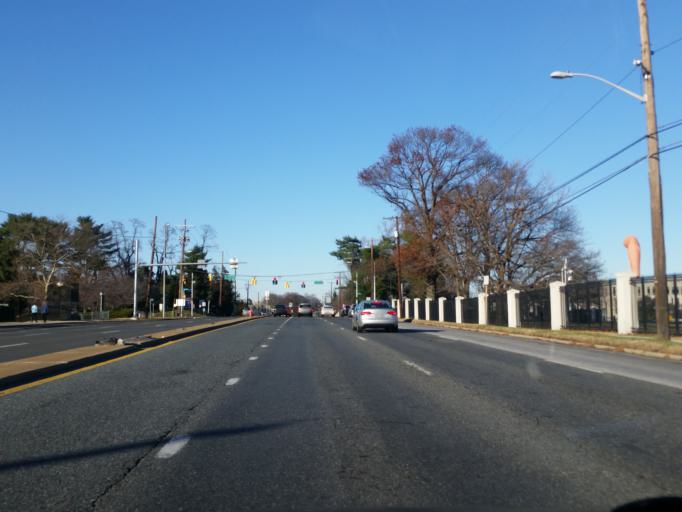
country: US
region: Maryland
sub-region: Montgomery County
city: Bethesda
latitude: 38.9984
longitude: -77.0967
